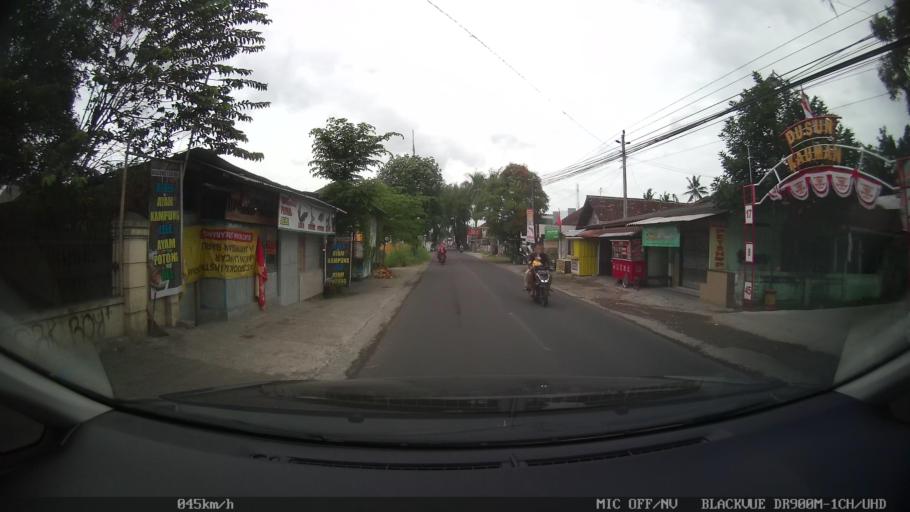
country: ID
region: Daerah Istimewa Yogyakarta
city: Sewon
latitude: -7.8636
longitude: 110.4083
